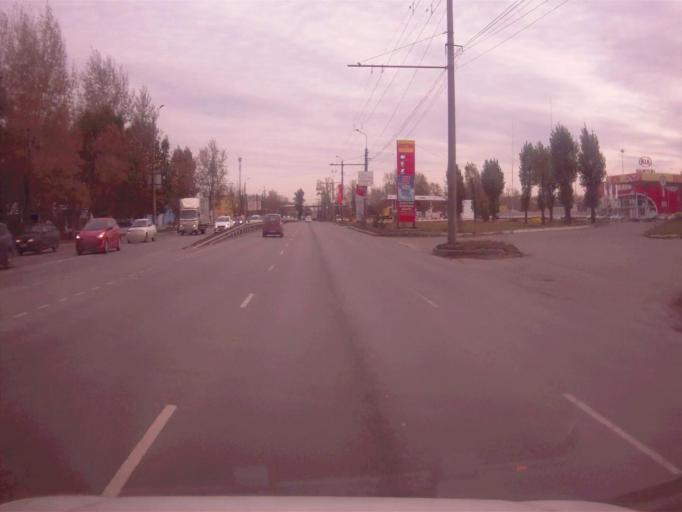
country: RU
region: Chelyabinsk
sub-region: Gorod Chelyabinsk
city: Chelyabinsk
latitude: 55.1364
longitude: 61.4625
